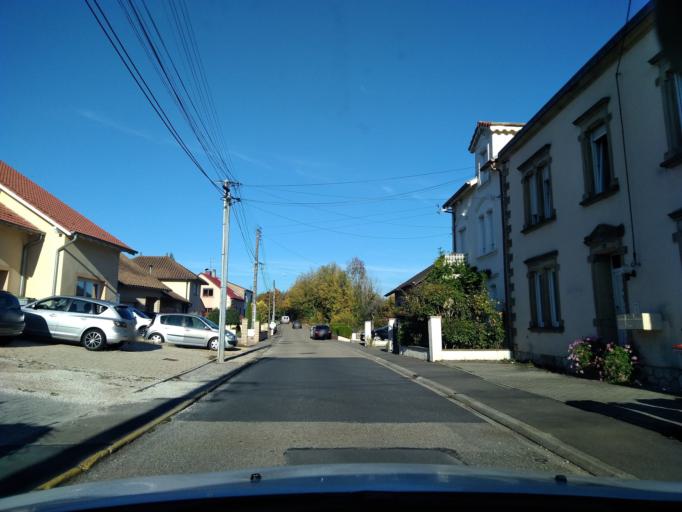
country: FR
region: Lorraine
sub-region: Departement de la Moselle
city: Remelfing
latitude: 49.0931
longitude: 7.0867
